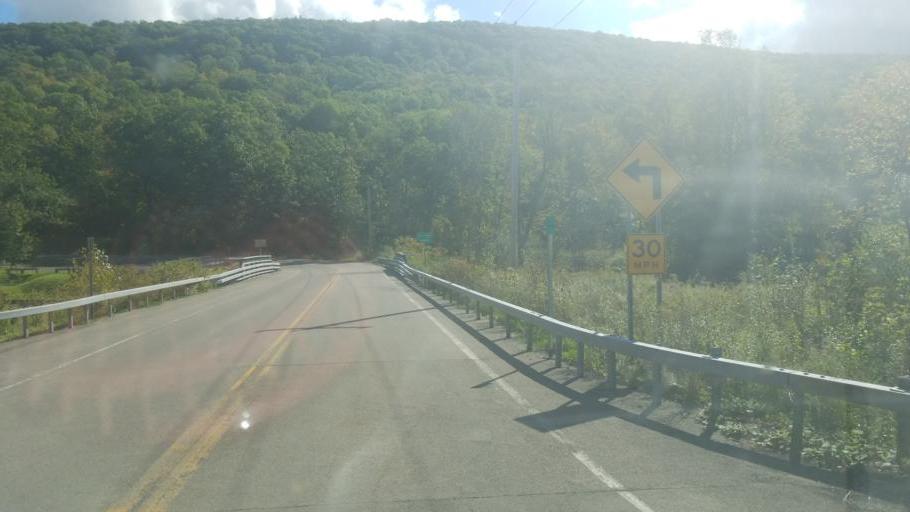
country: US
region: New York
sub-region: Allegany County
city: Cuba
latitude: 42.2365
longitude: -78.3080
